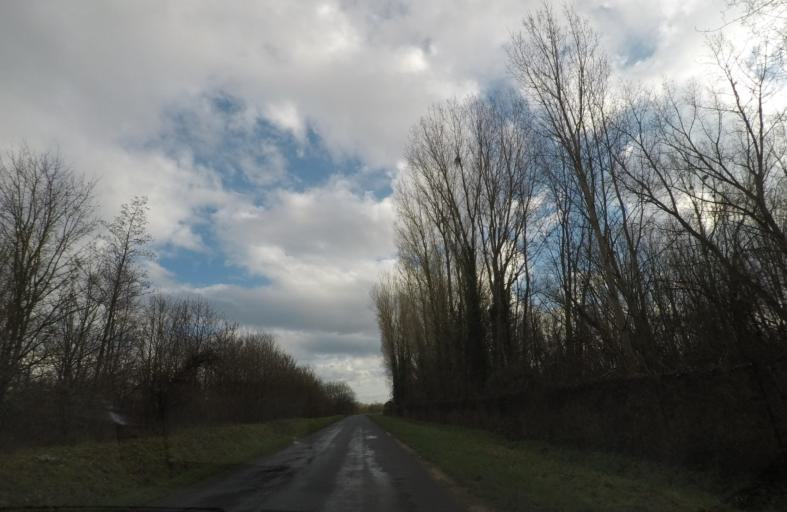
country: FR
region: Centre
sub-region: Departement du Cher
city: Bourges
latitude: 47.0488
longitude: 2.4140
